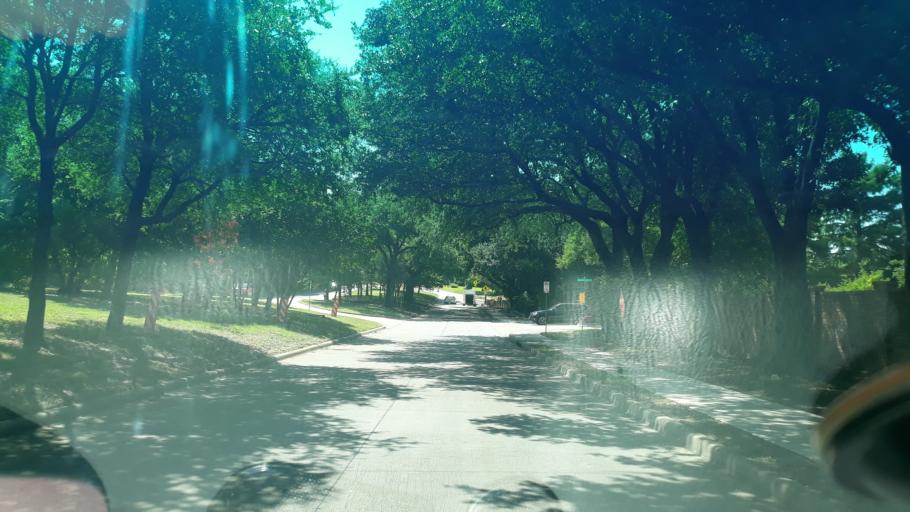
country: US
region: Texas
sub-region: Dallas County
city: Highland Park
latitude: 32.8138
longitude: -96.7239
